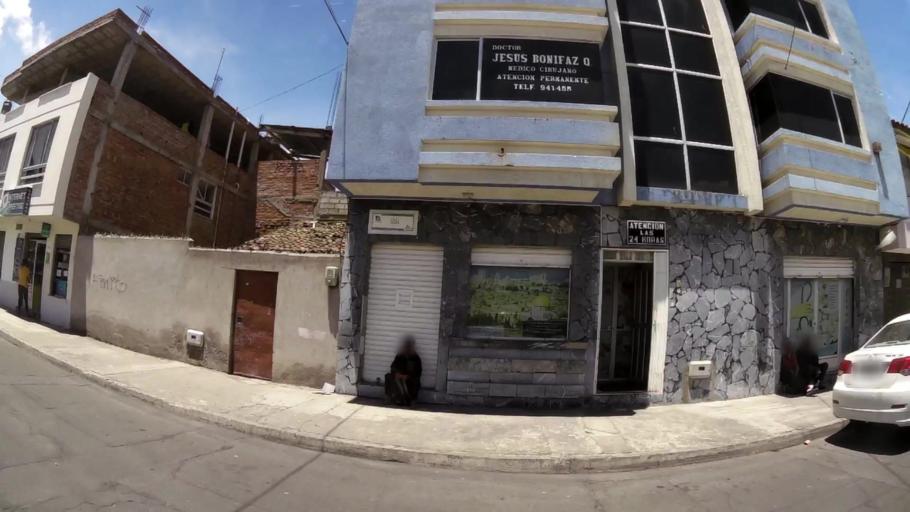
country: EC
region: Chimborazo
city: Riobamba
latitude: -1.6760
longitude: -78.6436
